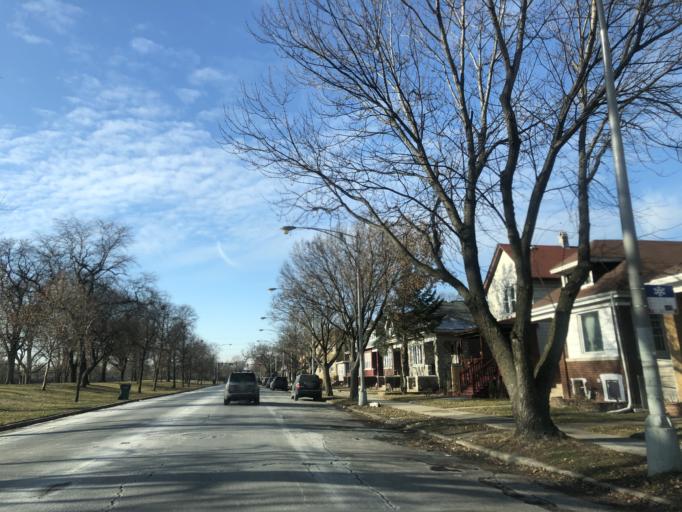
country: US
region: Illinois
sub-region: Cook County
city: Hometown
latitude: 41.7716
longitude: -87.7080
